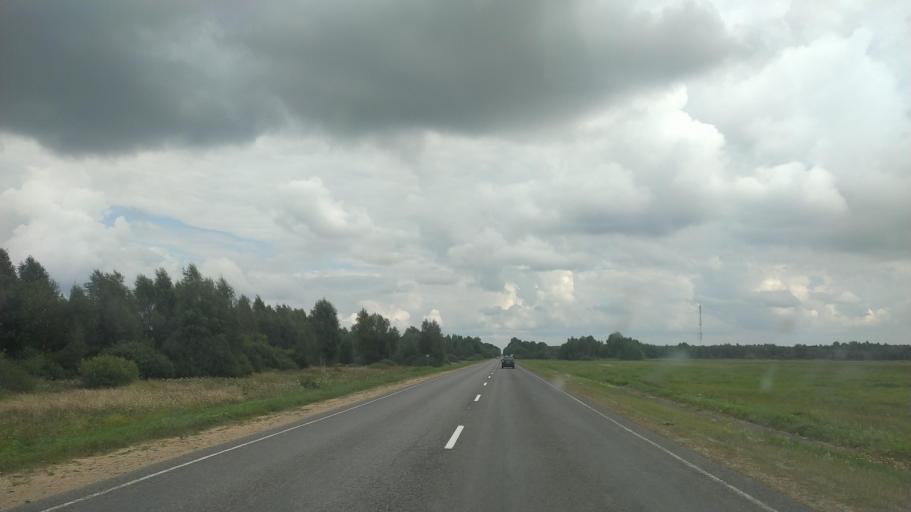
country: BY
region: Brest
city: Byaroza
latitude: 52.5529
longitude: 25.0219
